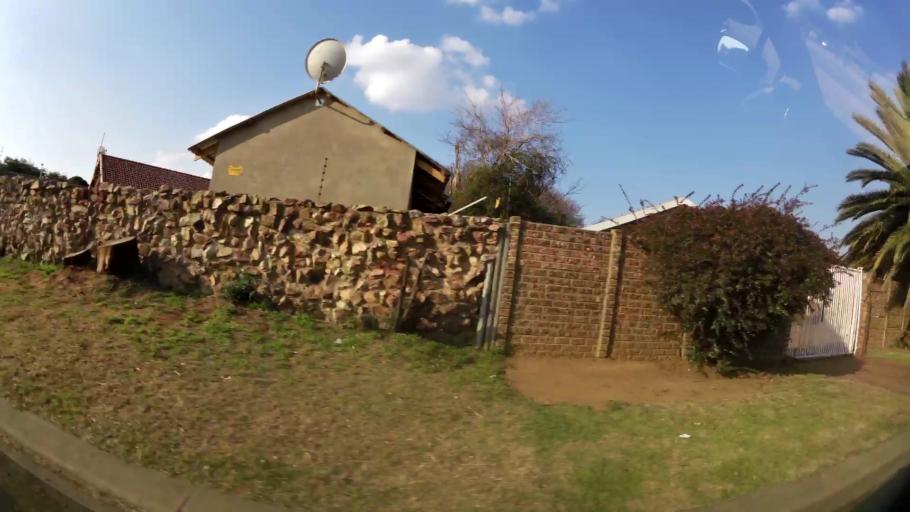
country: ZA
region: Gauteng
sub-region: Ekurhuleni Metropolitan Municipality
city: Benoni
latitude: -26.1307
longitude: 28.3764
